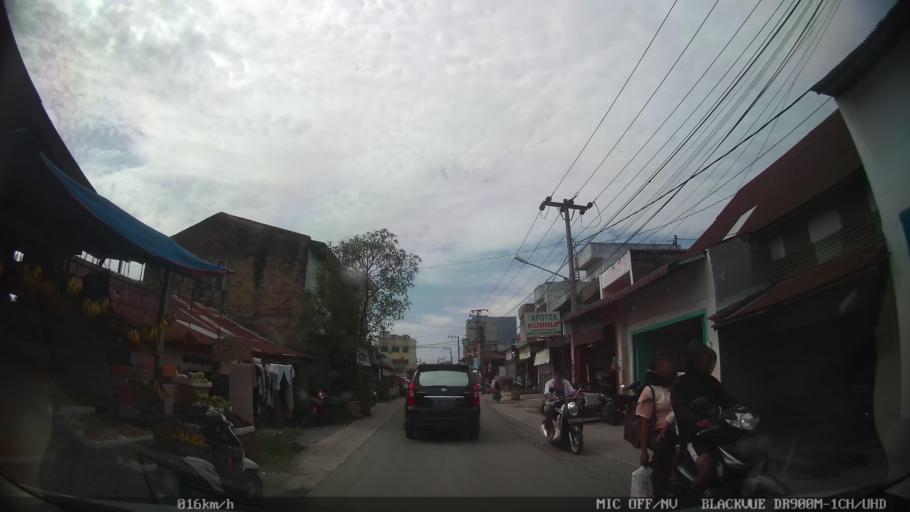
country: ID
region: North Sumatra
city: Percut
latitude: 3.6144
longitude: 98.8000
